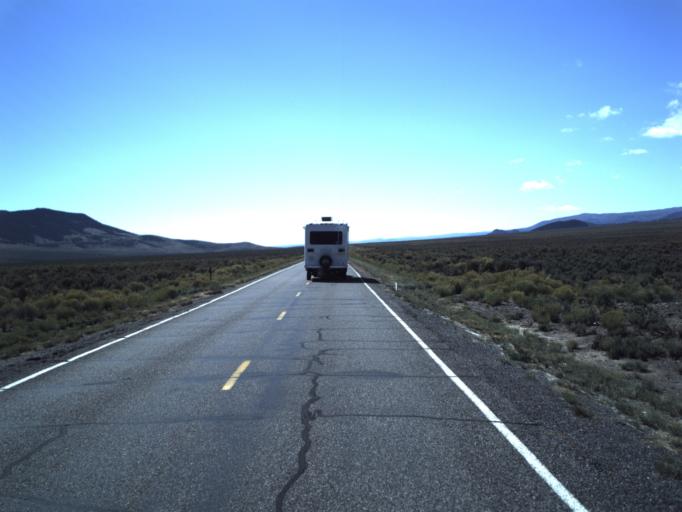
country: US
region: Utah
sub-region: Wayne County
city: Loa
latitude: 38.4037
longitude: -111.9286
